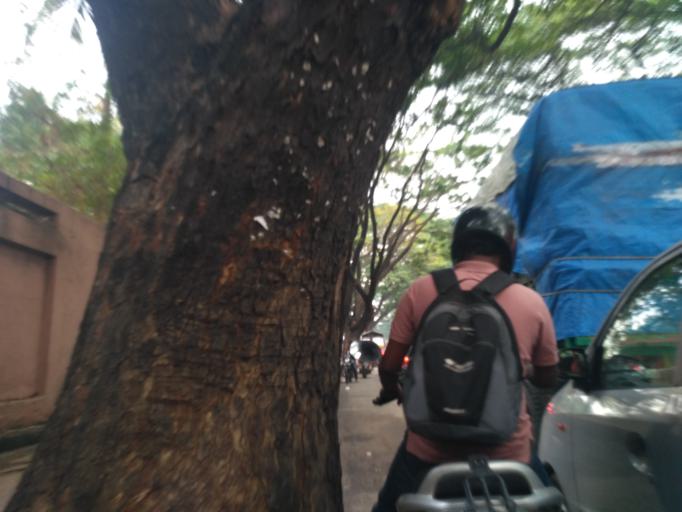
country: IN
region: Karnataka
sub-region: Bangalore Urban
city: Bangalore
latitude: 13.0272
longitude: 77.5353
